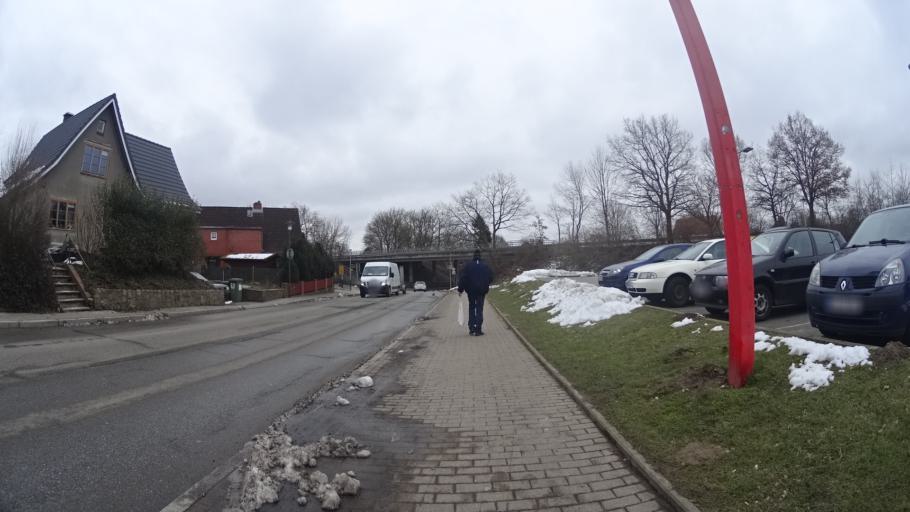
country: DE
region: Schleswig-Holstein
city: Lutjenburg
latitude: 54.2887
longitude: 10.5829
